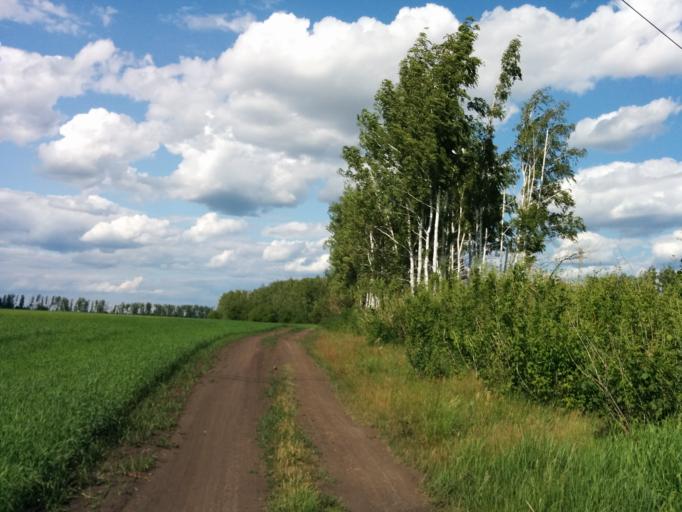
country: RU
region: Tambov
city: Tambov
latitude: 52.7974
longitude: 41.3831
